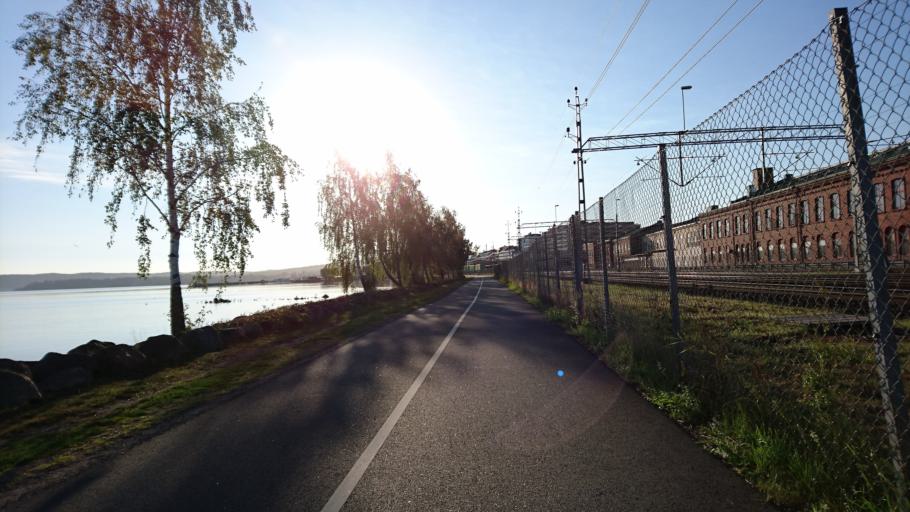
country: SE
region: Joenkoeping
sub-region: Jonkopings Kommun
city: Jonkoping
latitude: 57.7862
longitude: 14.1560
